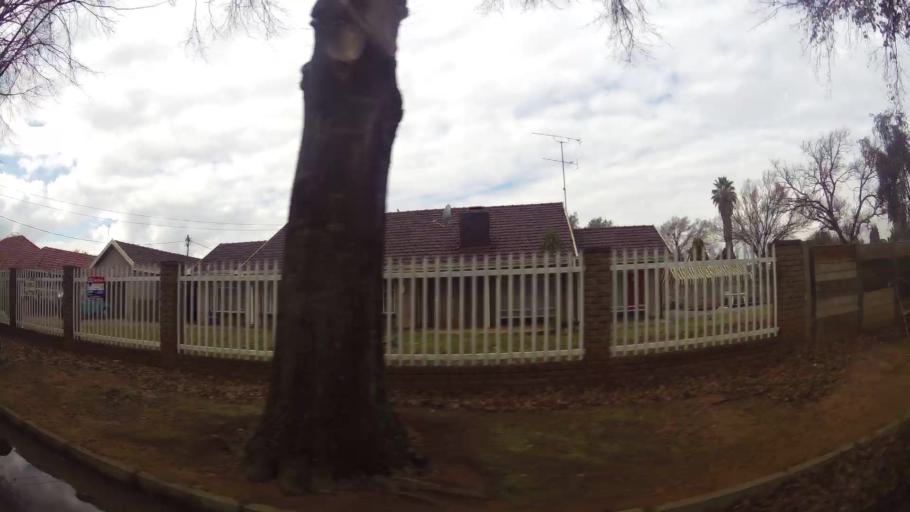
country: ZA
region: Gauteng
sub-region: Sedibeng District Municipality
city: Vereeniging
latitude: -26.6422
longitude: 27.9750
